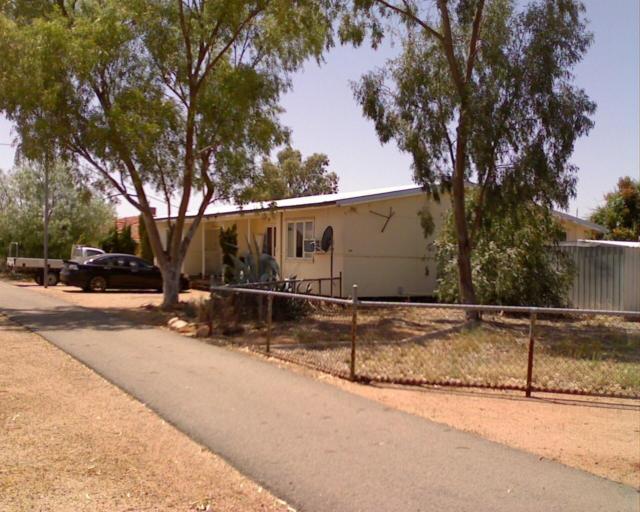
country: AU
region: Western Australia
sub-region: Merredin
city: Merredin
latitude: -30.9169
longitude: 118.2041
